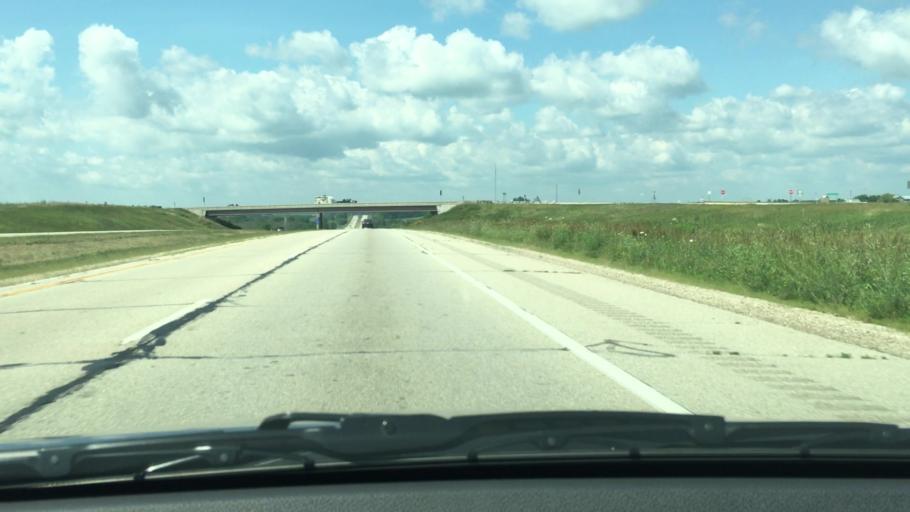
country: US
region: Wisconsin
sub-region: Dodge County
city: Theresa
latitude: 43.4703
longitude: -88.3665
